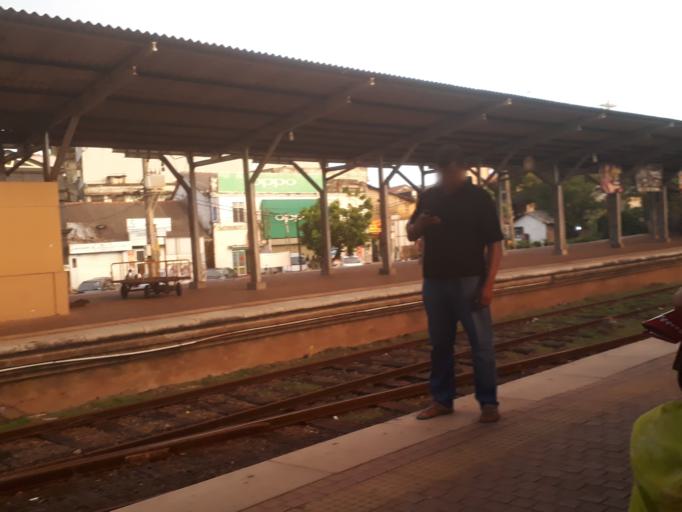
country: LK
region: Southern
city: Galle
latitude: 6.0339
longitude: 80.2143
